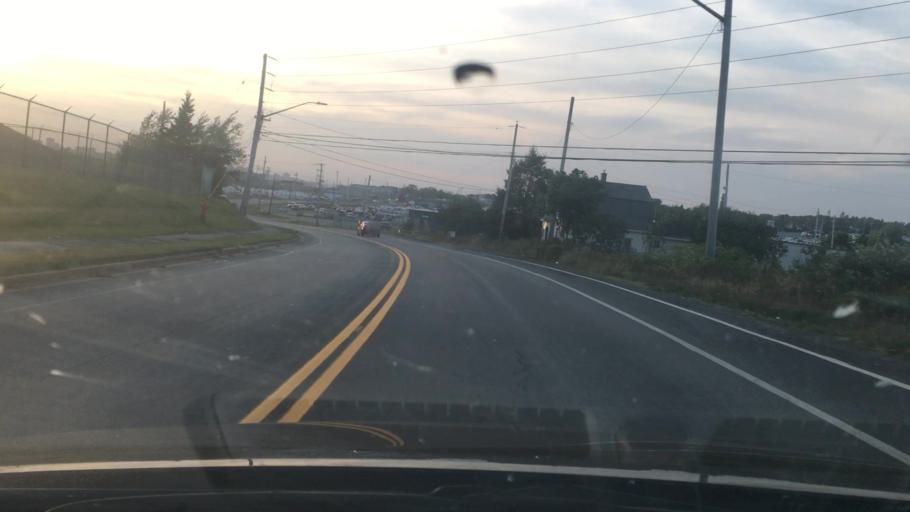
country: CA
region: Nova Scotia
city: Cole Harbour
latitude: 44.6195
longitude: -63.5036
